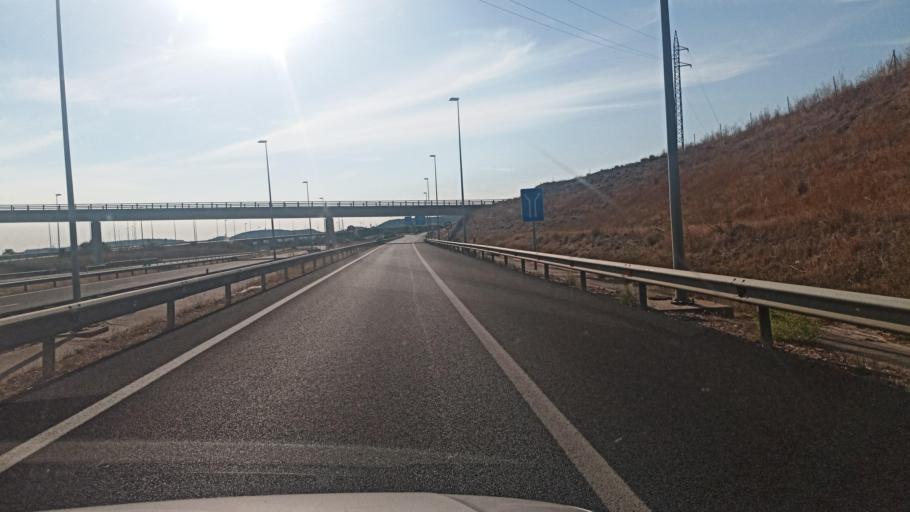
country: ES
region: Castille and Leon
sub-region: Provincia de Burgos
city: Hurones
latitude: 42.3714
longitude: -3.6286
